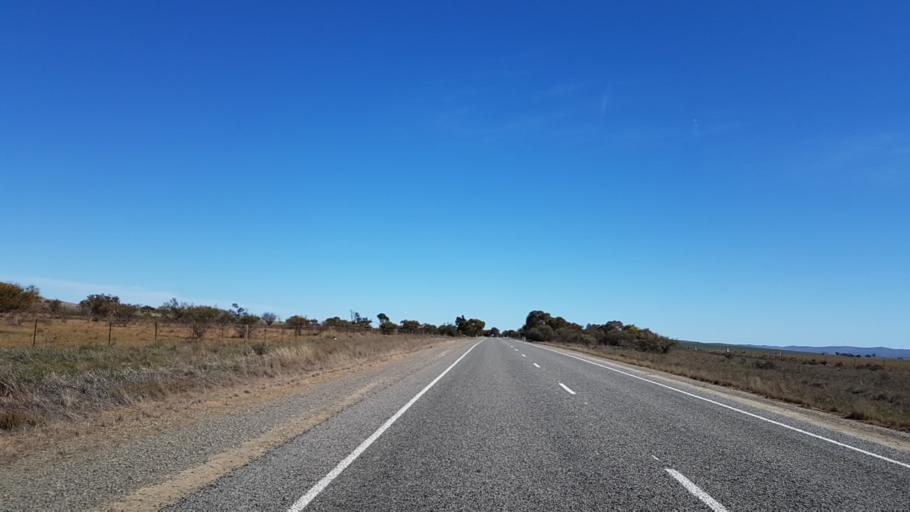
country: AU
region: South Australia
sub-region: Peterborough
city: Peterborough
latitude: -33.2396
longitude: 138.8761
